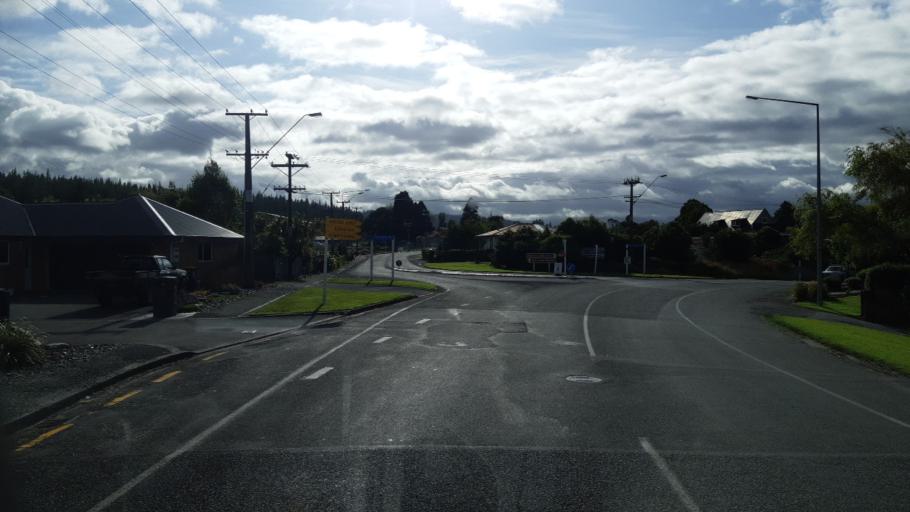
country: NZ
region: West Coast
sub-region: Westland District
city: Hokitika
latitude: -42.7480
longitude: 171.0074
